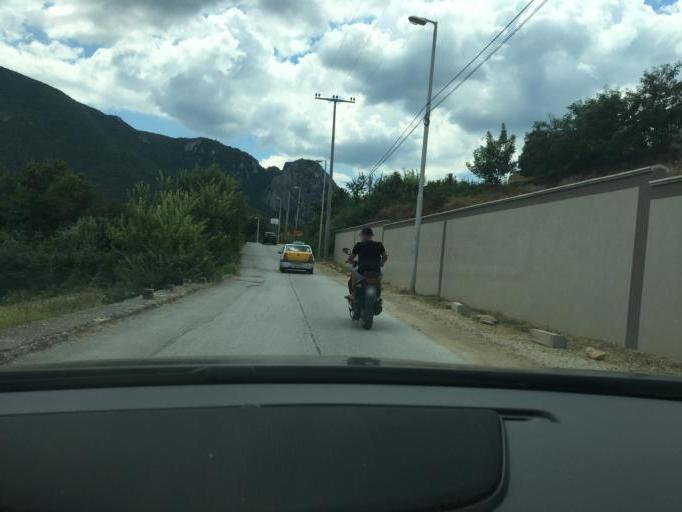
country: MK
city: Ljubin
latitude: 41.9763
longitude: 21.3027
